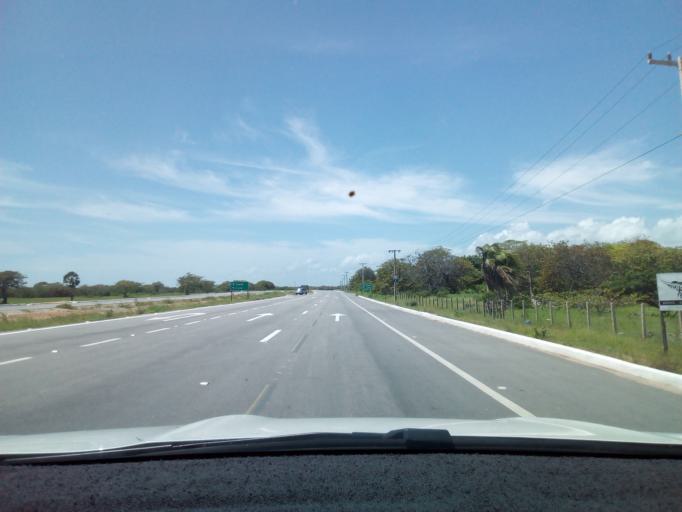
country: BR
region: Ceara
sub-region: Aracati
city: Aracati
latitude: -4.4547
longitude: -37.8090
